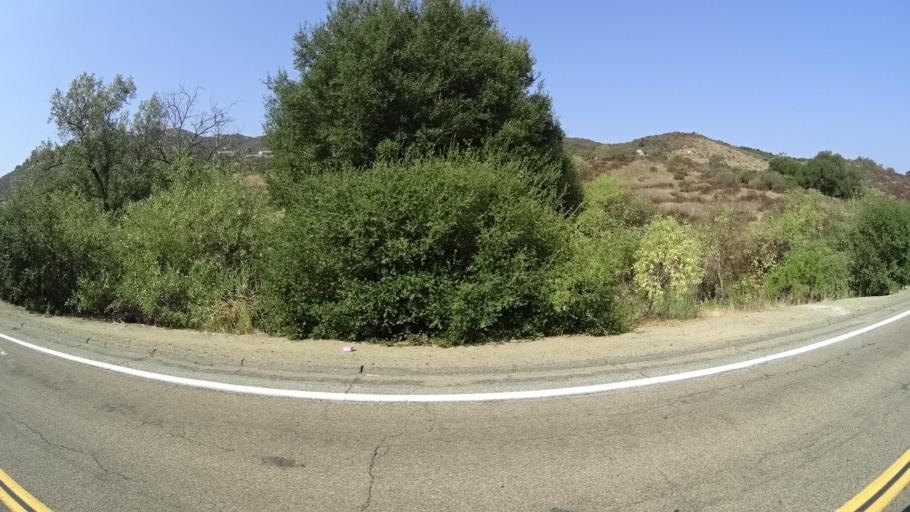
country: US
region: California
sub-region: San Diego County
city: Hidden Meadows
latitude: 33.2357
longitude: -117.1463
